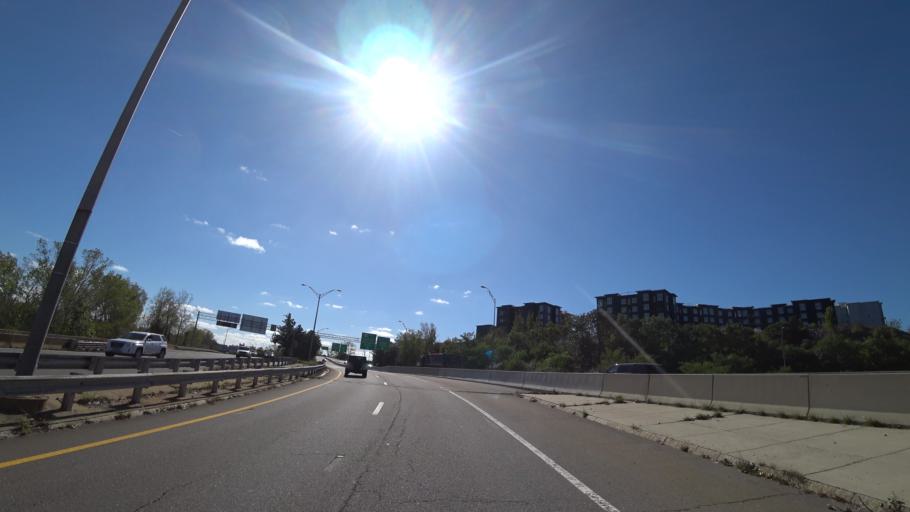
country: US
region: Massachusetts
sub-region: Norfolk County
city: Braintree
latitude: 42.2316
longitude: -71.0112
